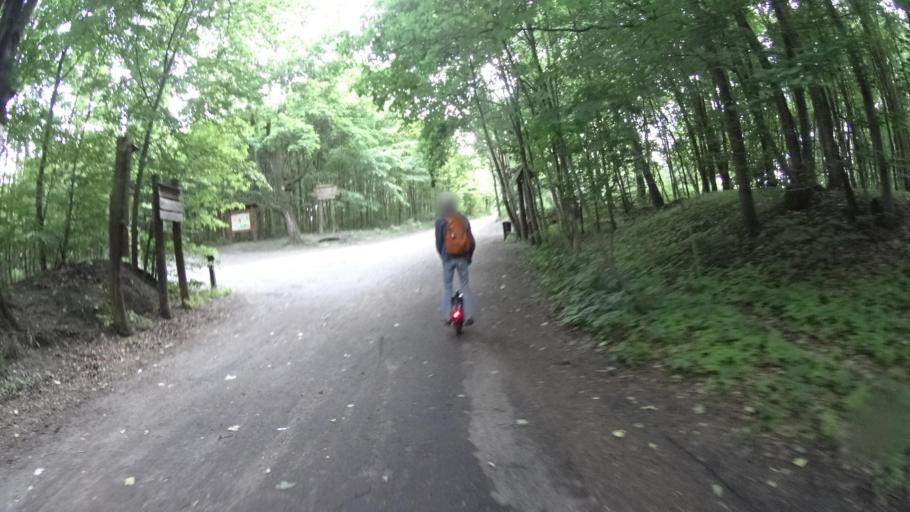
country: PL
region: Masovian Voivodeship
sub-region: Warszawa
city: Kabaty
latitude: 52.1179
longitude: 21.0862
